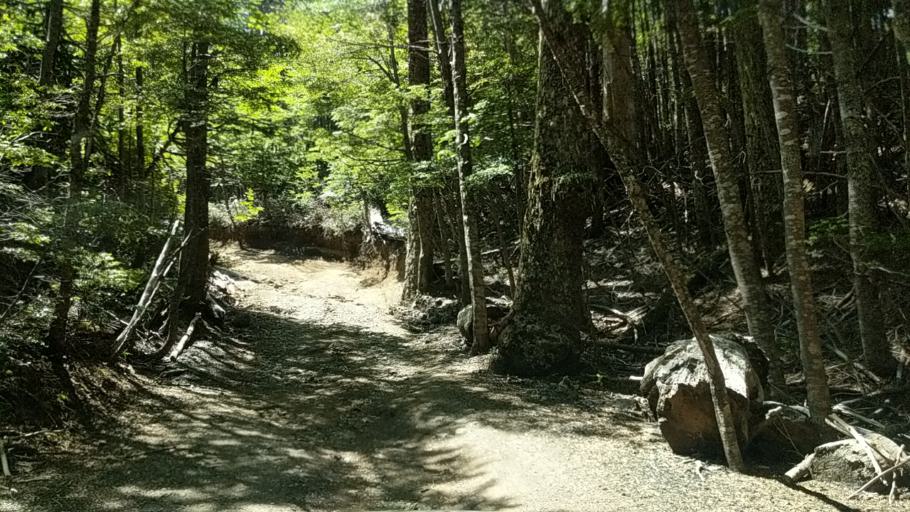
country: CL
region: Araucania
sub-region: Provincia de Cautin
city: Pucon
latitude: -39.4615
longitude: -71.8520
